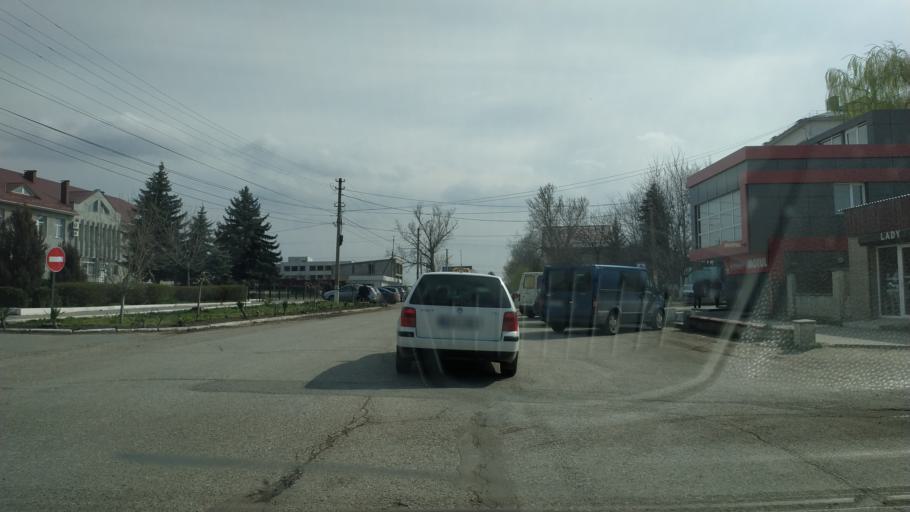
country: MD
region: Gagauzia
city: Vulcanesti
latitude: 45.6830
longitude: 28.4070
